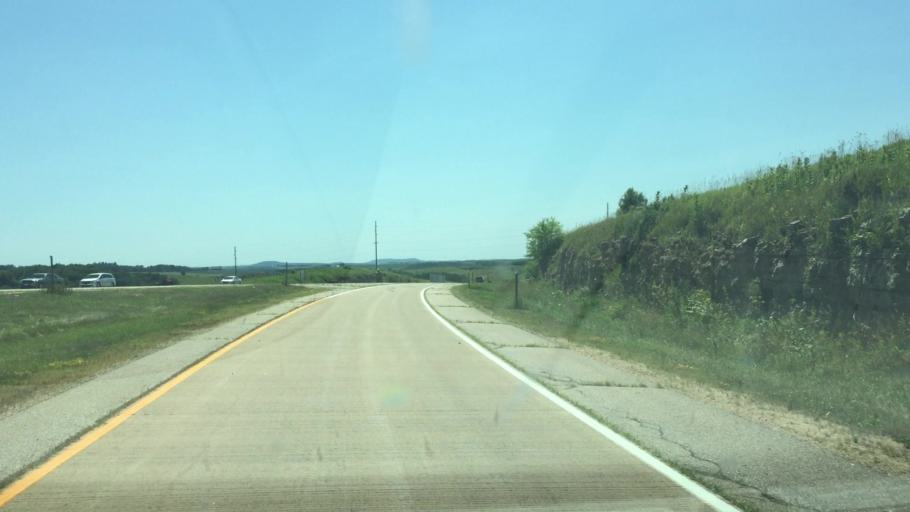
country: US
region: Wisconsin
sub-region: Iowa County
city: Mineral Point
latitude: 42.8853
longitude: -90.1690
